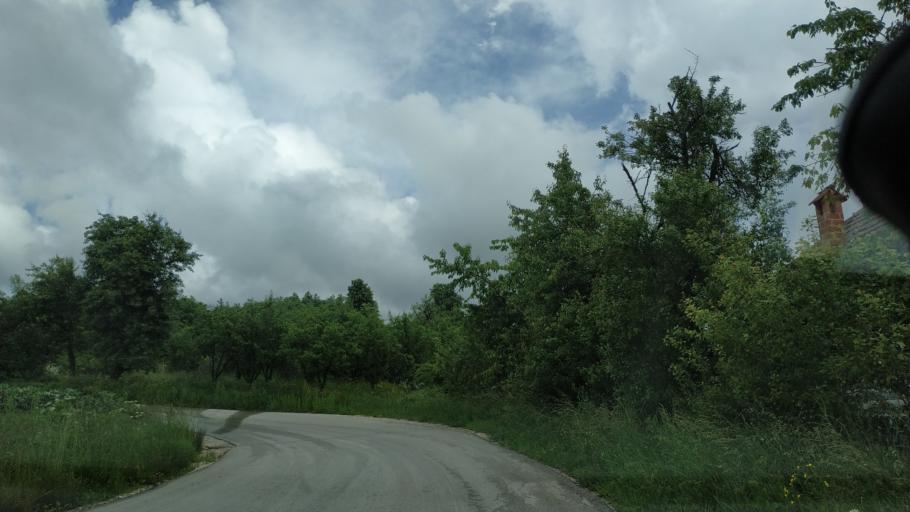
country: RS
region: Central Serbia
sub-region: Zajecarski Okrug
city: Soko Banja
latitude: 43.6840
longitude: 21.9341
